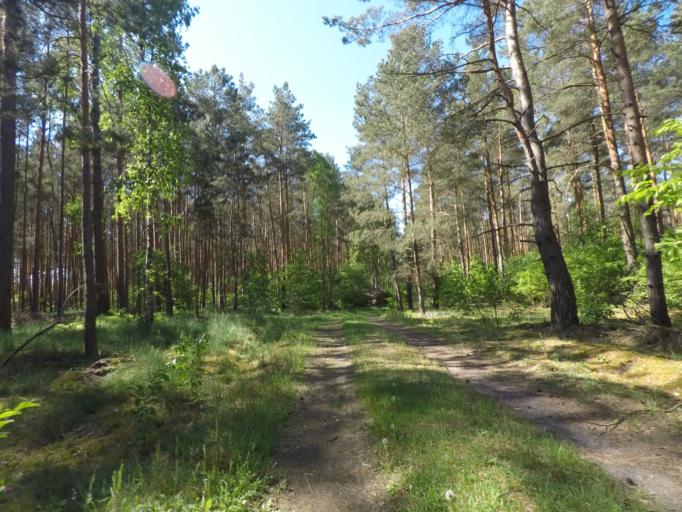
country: DE
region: Brandenburg
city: Melchow
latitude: 52.8254
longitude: 13.7469
